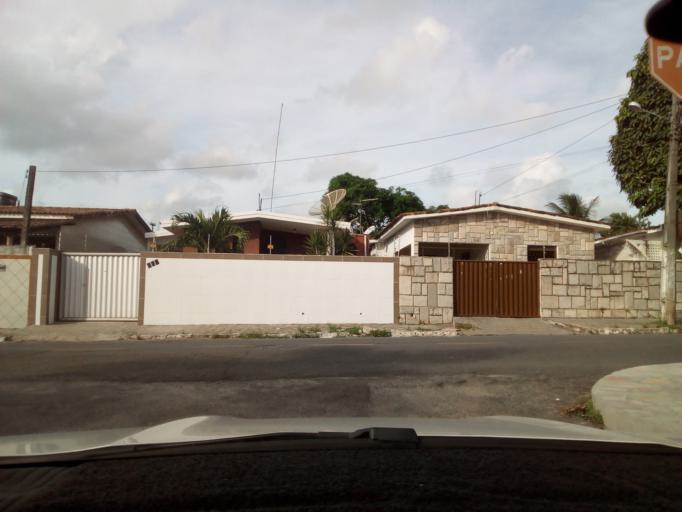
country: BR
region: Paraiba
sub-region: Joao Pessoa
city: Joao Pessoa
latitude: -7.1522
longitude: -34.8768
